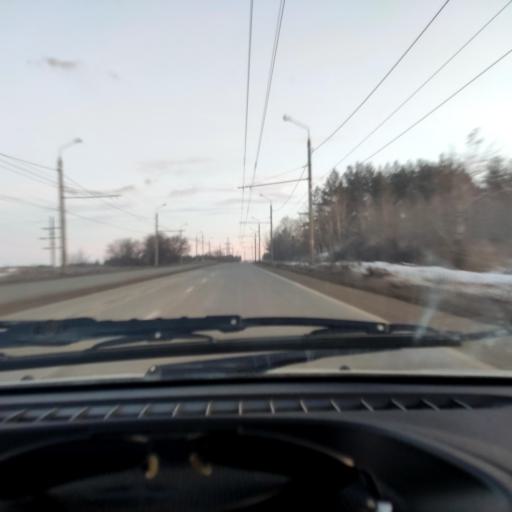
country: RU
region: Samara
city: Zhigulevsk
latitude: 53.5053
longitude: 49.5167
